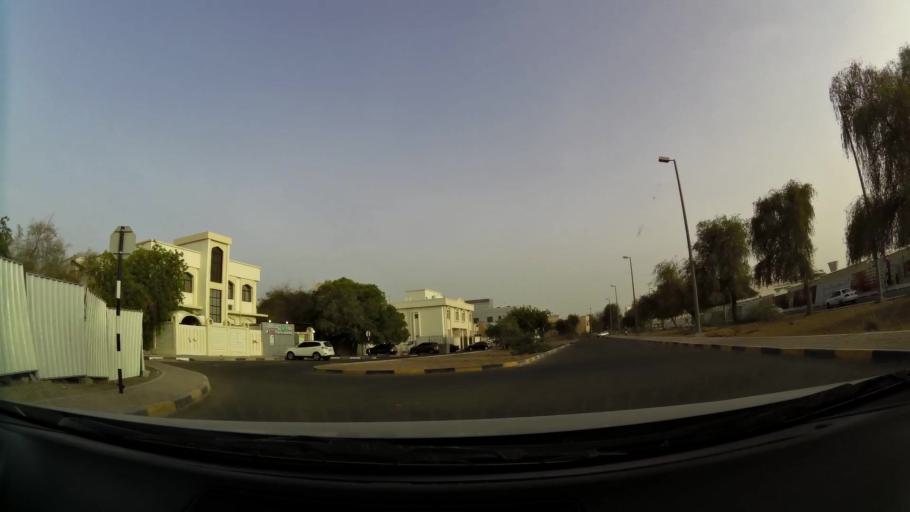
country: AE
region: Abu Dhabi
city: Al Ain
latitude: 24.2467
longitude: 55.7287
